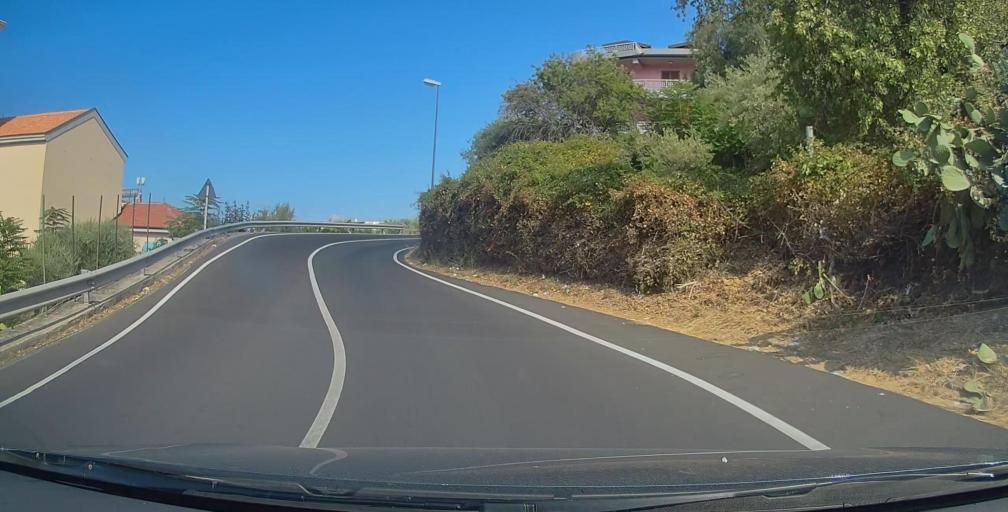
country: IT
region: Sicily
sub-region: Messina
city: Patti
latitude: 38.1513
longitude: 14.9676
